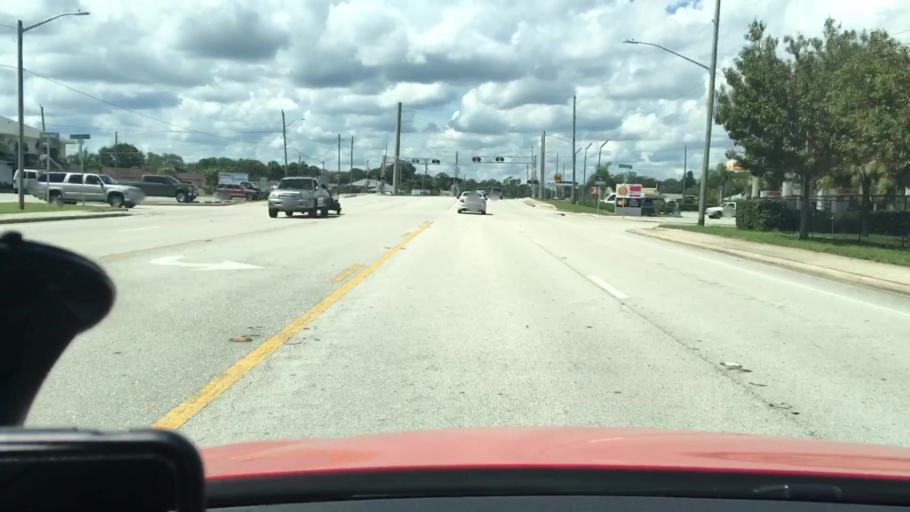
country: US
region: Florida
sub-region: Volusia County
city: Edgewater
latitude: 28.9703
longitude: -80.9012
